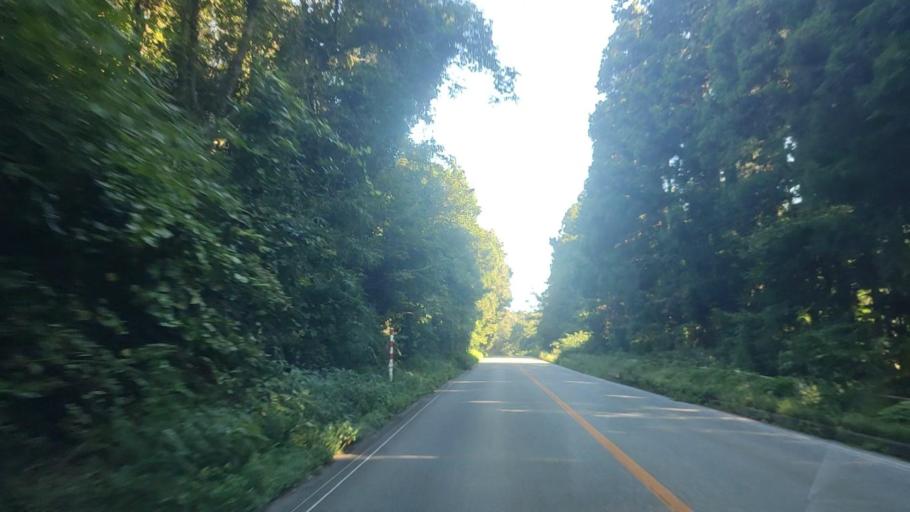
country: JP
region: Ishikawa
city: Nanao
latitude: 37.1041
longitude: 136.9477
